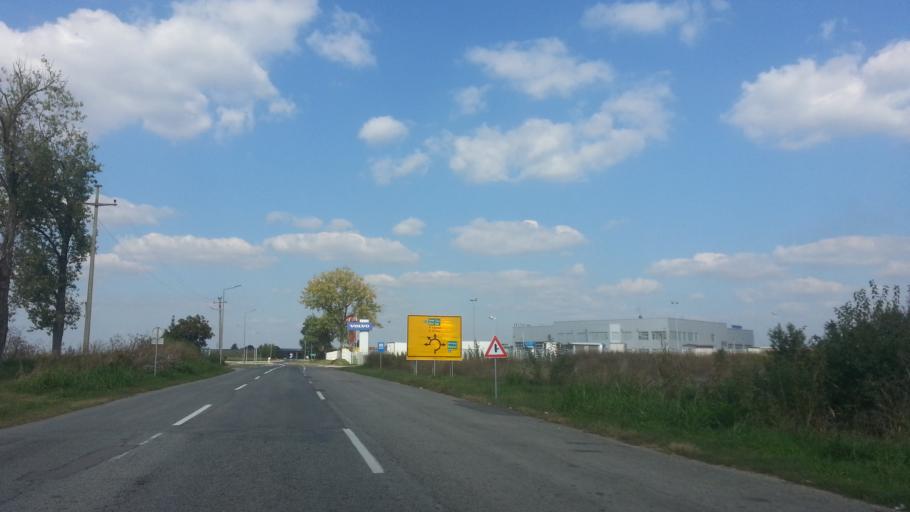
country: RS
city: Novi Banovci
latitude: 44.9396
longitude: 20.2812
